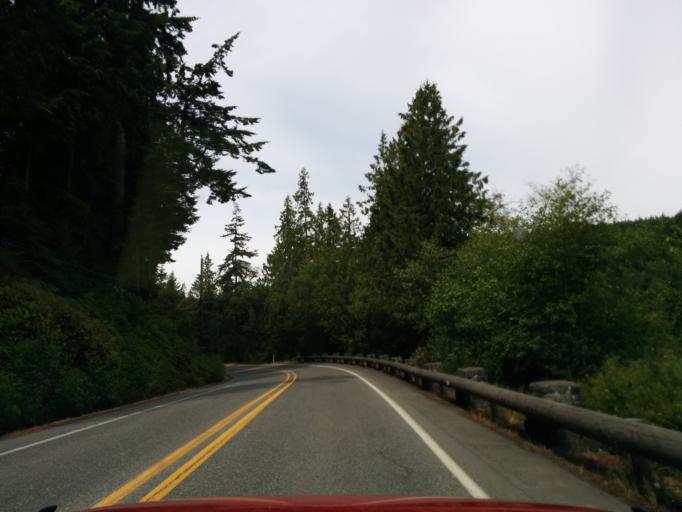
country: US
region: Washington
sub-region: Island County
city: Ault Field
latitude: 48.4173
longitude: -122.6380
